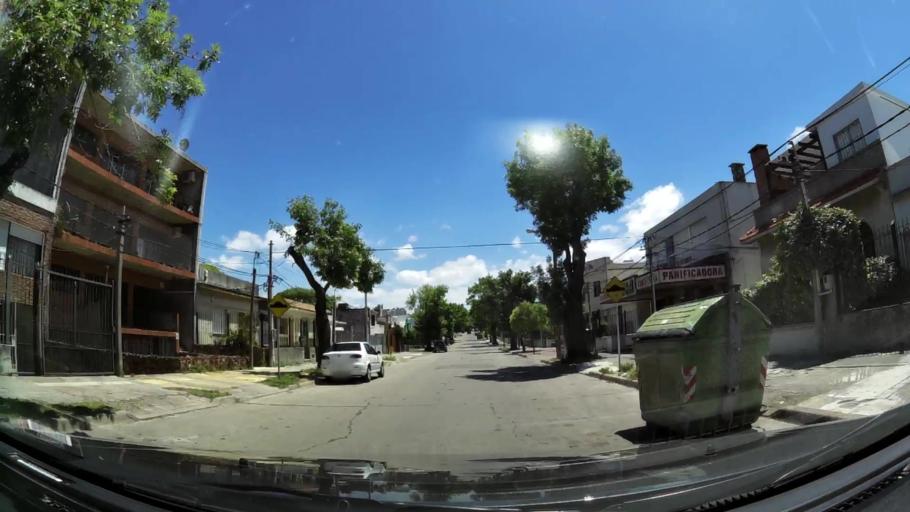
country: UY
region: Montevideo
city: Montevideo
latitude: -34.8929
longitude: -56.1426
